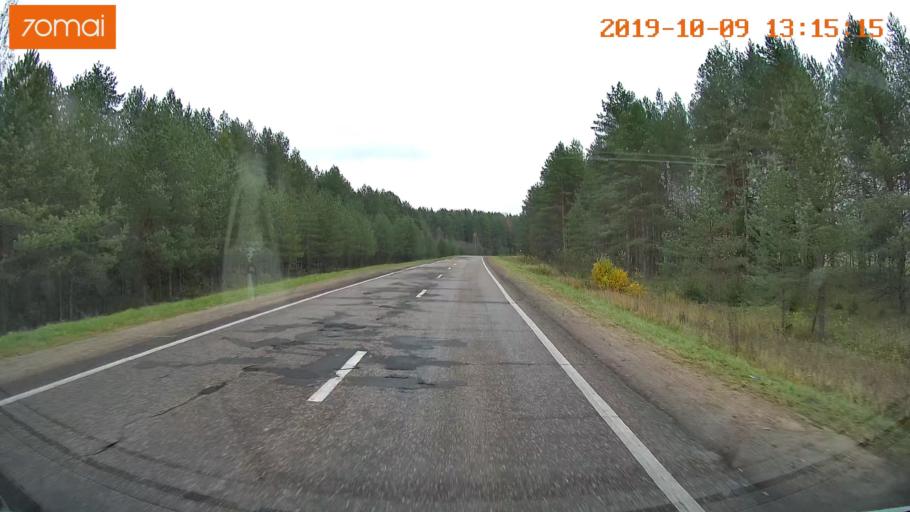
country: RU
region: Jaroslavl
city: Lyubim
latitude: 58.3681
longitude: 40.7488
